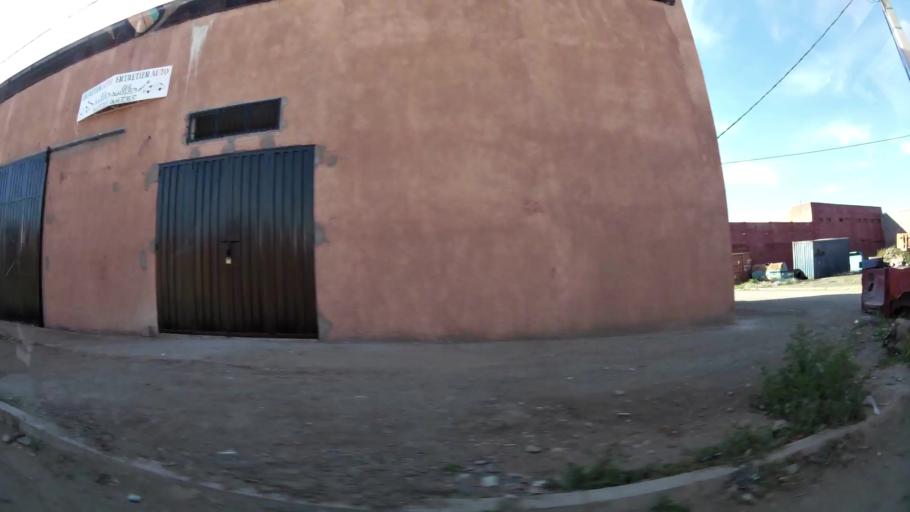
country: MA
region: Marrakech-Tensift-Al Haouz
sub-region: Marrakech
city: Marrakesh
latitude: 31.6842
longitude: -8.0584
